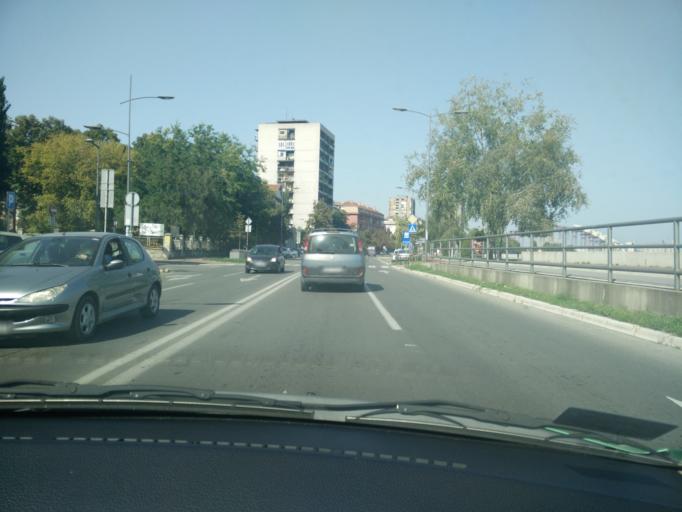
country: RS
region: Autonomna Pokrajina Vojvodina
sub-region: Juznobacki Okrug
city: Novi Sad
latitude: 45.2557
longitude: 19.8550
